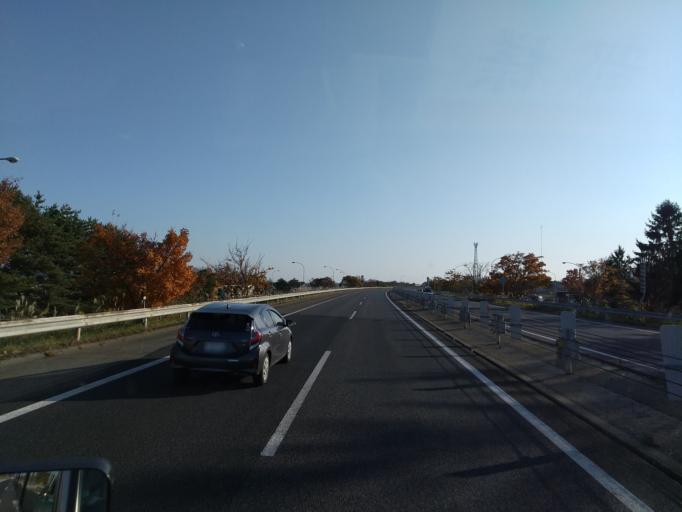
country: JP
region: Iwate
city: Morioka-shi
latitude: 39.6207
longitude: 141.1297
